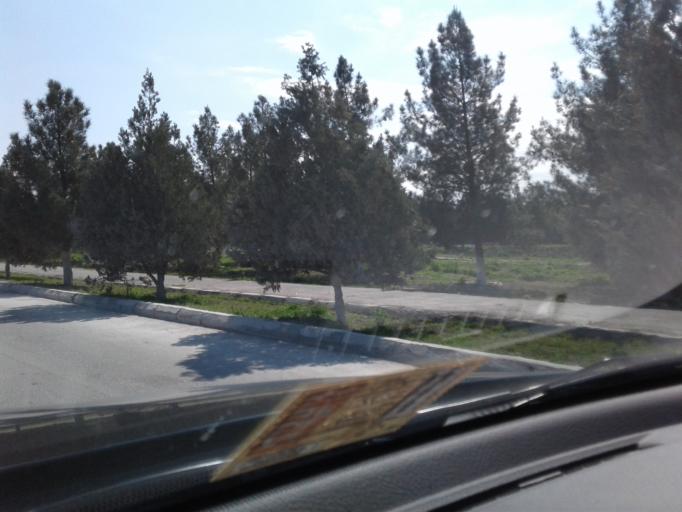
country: TM
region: Ahal
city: Abadan
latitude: 38.0644
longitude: 58.2563
